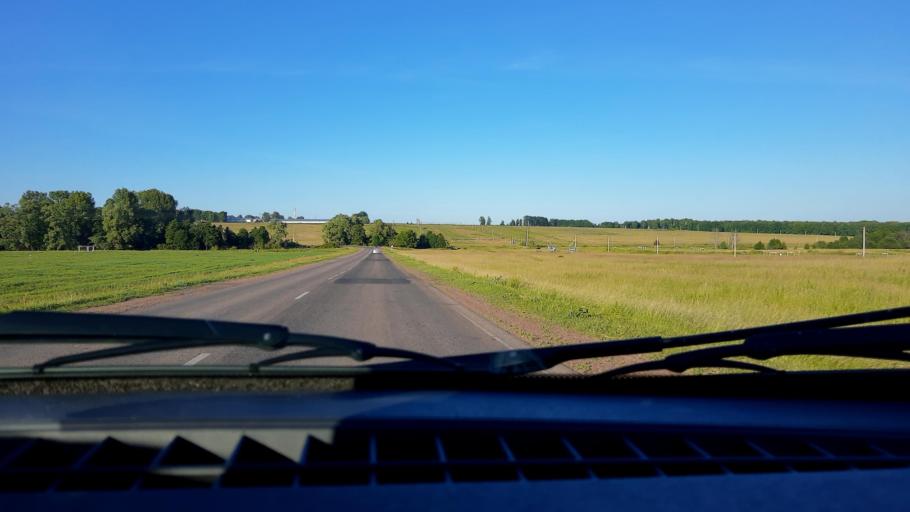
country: RU
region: Bashkortostan
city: Mikhaylovka
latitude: 54.8266
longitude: 55.7748
